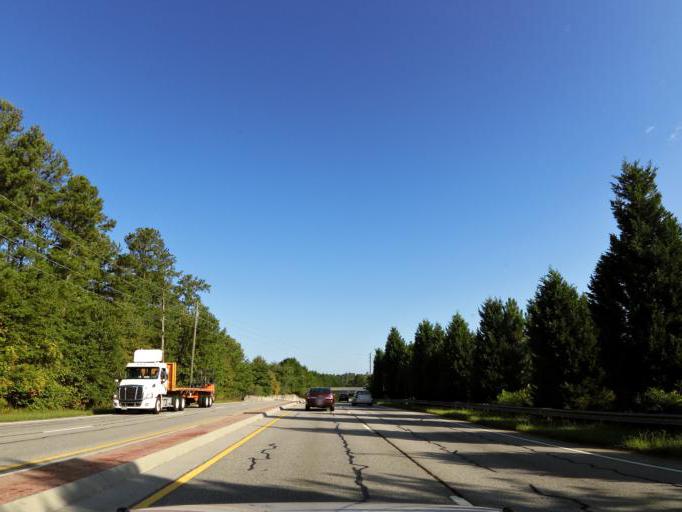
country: US
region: Georgia
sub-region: Cobb County
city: Powder Springs
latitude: 33.9214
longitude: -84.6292
